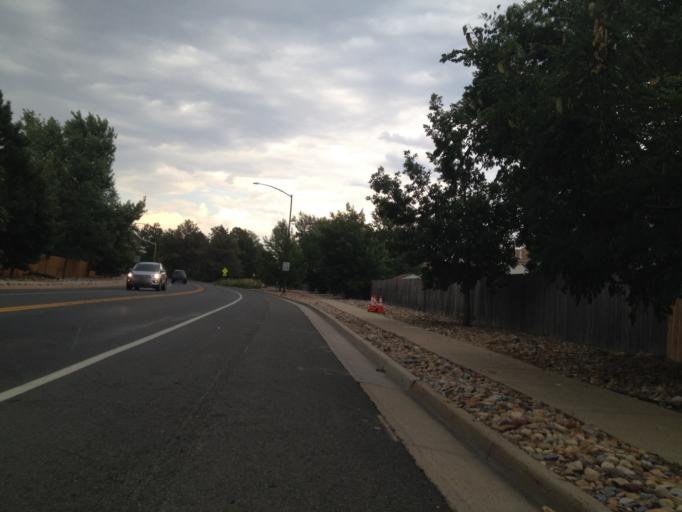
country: US
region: Colorado
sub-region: Boulder County
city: Louisville
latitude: 39.9687
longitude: -105.1373
